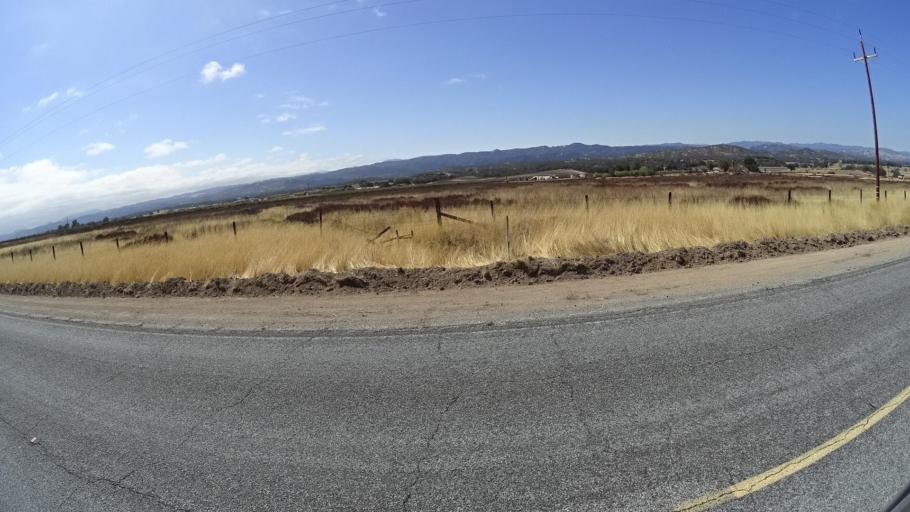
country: US
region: California
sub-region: San Luis Obispo County
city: Lake Nacimiento
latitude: 35.9256
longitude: -121.0412
